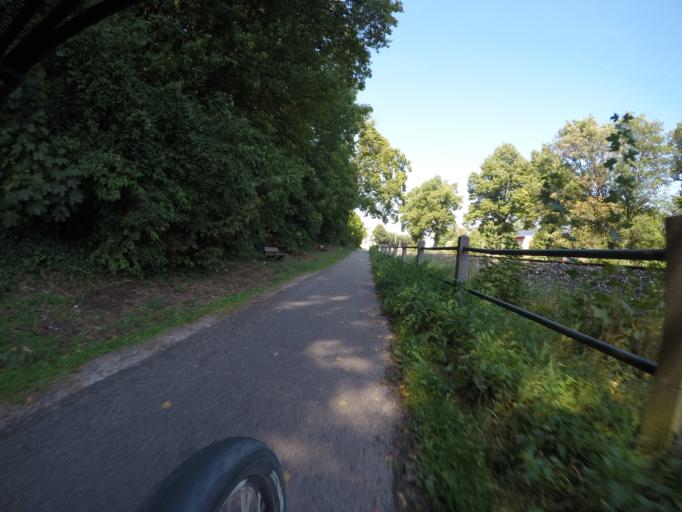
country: AT
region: Lower Austria
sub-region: Politischer Bezirk Baden
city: Berndorf
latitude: 47.9427
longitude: 16.1109
